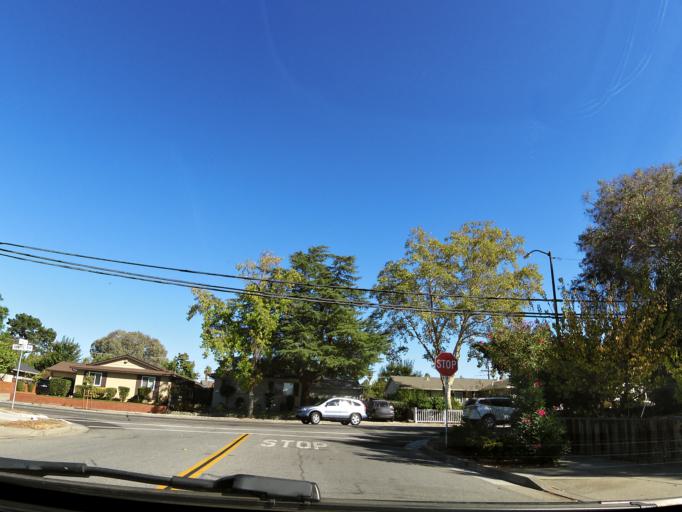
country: US
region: California
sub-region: Santa Clara County
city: Campbell
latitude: 37.2736
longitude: -121.9646
